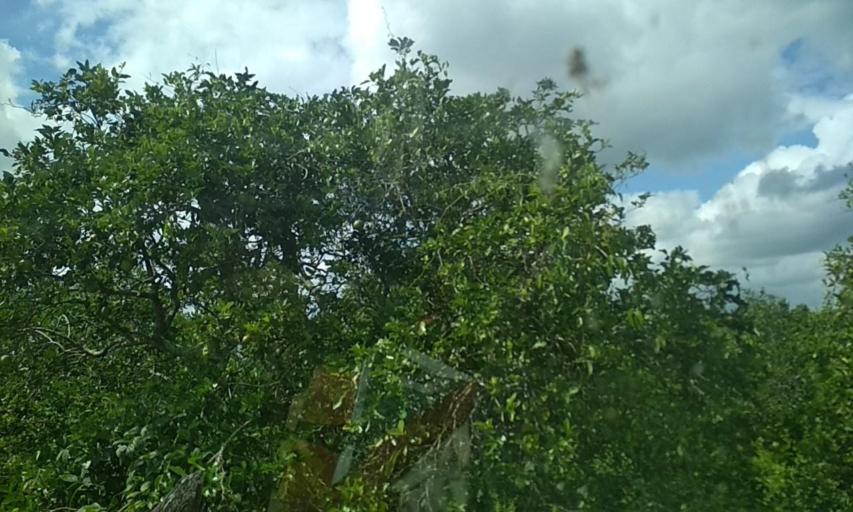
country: MX
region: Puebla
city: San Jose Acateno
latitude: 20.2842
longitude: -97.1283
